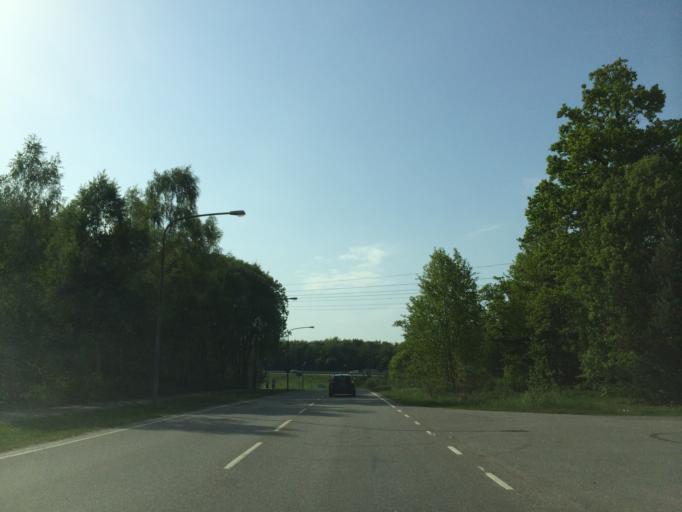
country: SE
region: Stockholm
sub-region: Nacka Kommun
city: Alta
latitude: 59.2632
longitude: 18.1465
